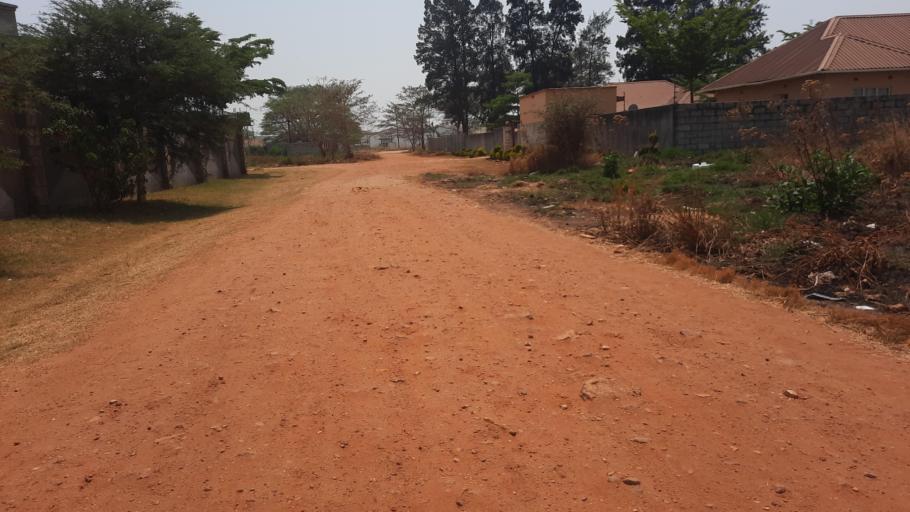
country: ZM
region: Lusaka
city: Lusaka
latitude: -15.3937
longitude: 28.3916
